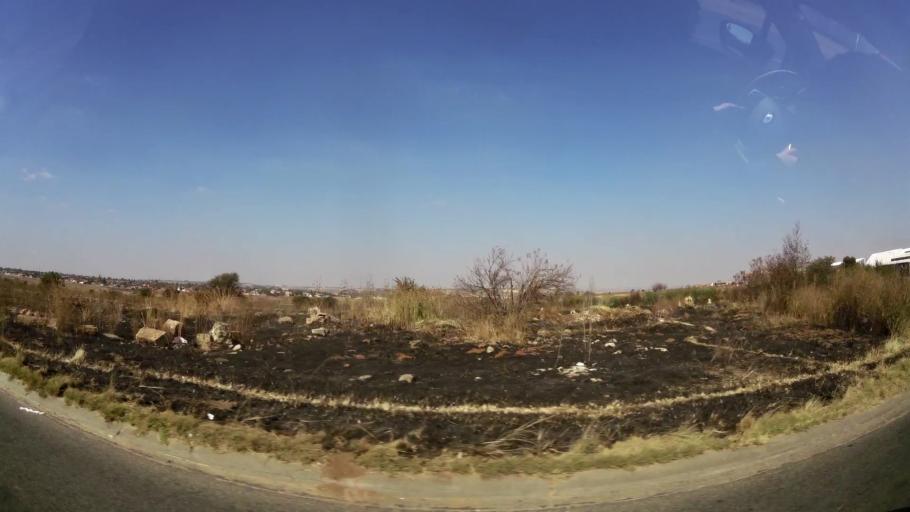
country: ZA
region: Gauteng
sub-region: City of Johannesburg Metropolitan Municipality
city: Roodepoort
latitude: -26.1571
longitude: 27.8050
